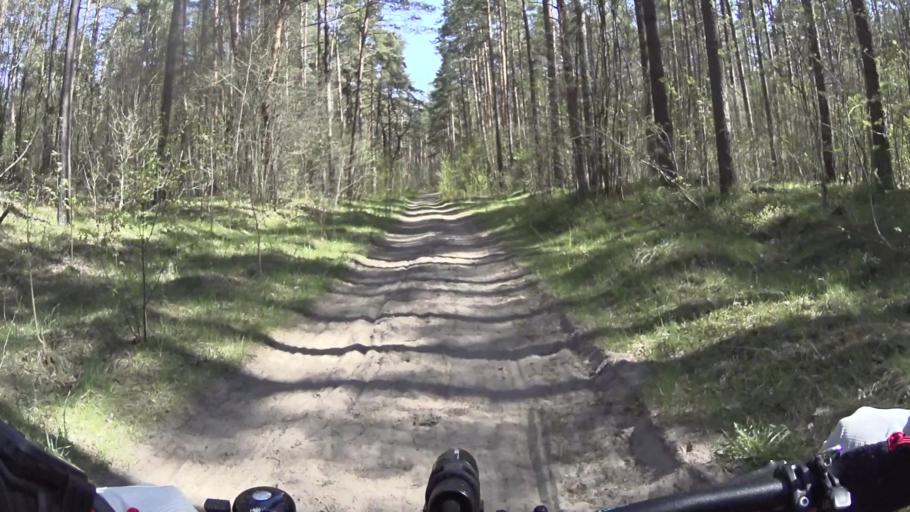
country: LV
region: Riga
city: Daugavgriva
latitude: 56.9818
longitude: 24.0059
